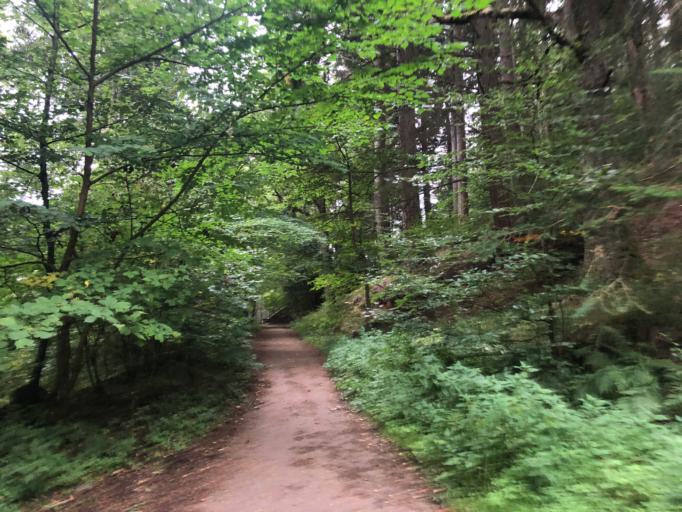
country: GB
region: Scotland
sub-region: Perth and Kinross
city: Pitlochry
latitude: 56.7287
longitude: -3.7764
